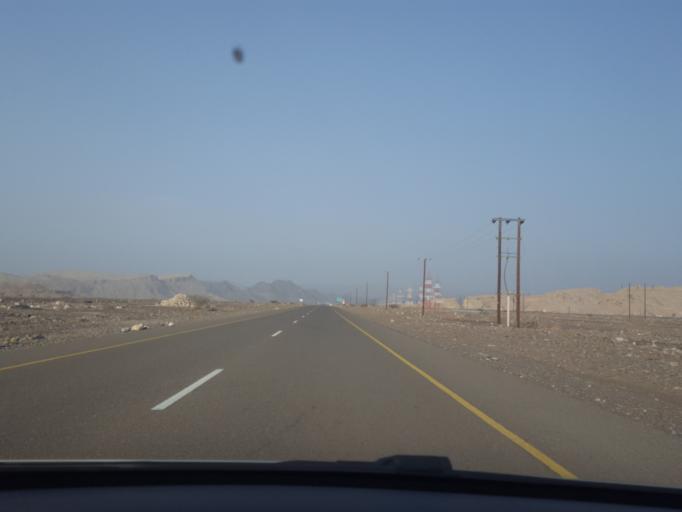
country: AE
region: Abu Dhabi
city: Al Ain
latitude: 24.0357
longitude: 56.0101
